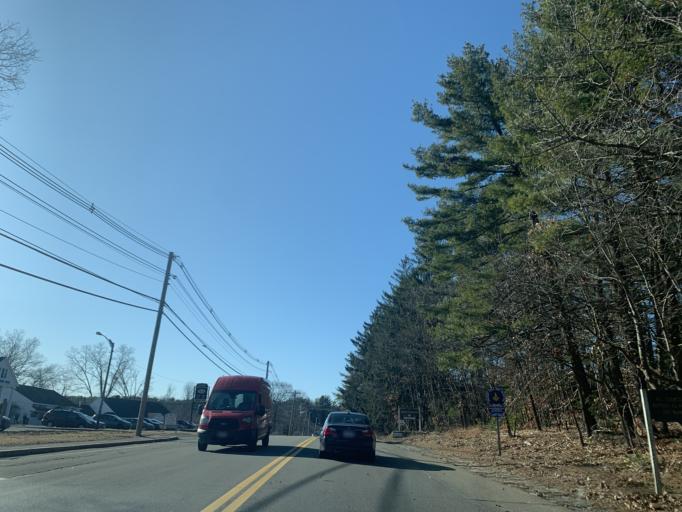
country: US
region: Massachusetts
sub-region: Worcester County
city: Southborough
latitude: 42.3518
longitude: -71.4871
